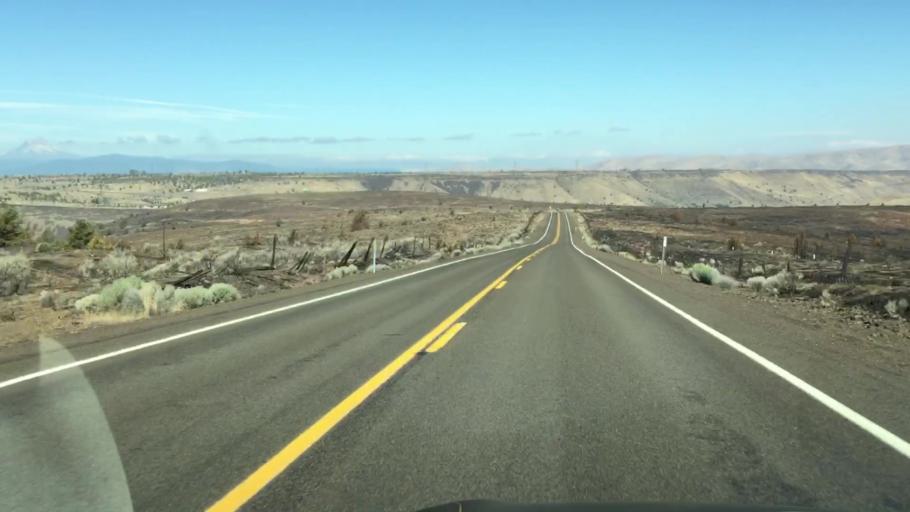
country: US
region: Oregon
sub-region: Jefferson County
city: Warm Springs
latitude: 45.1530
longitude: -121.0640
